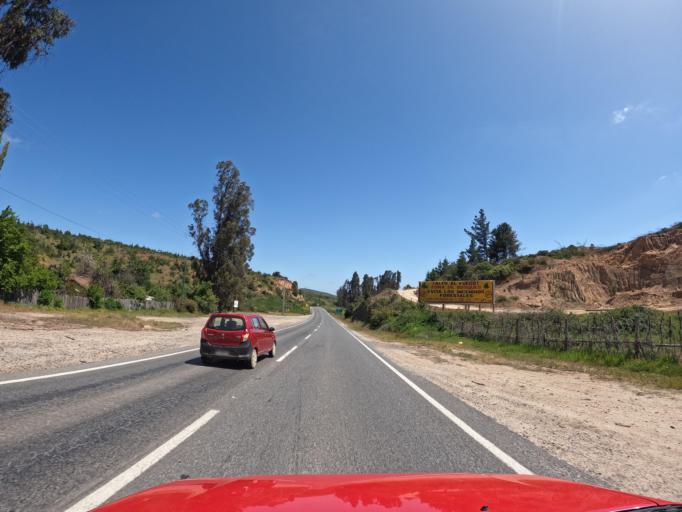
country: CL
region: O'Higgins
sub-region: Provincia de Colchagua
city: Santa Cruz
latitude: -34.6774
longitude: -71.7991
